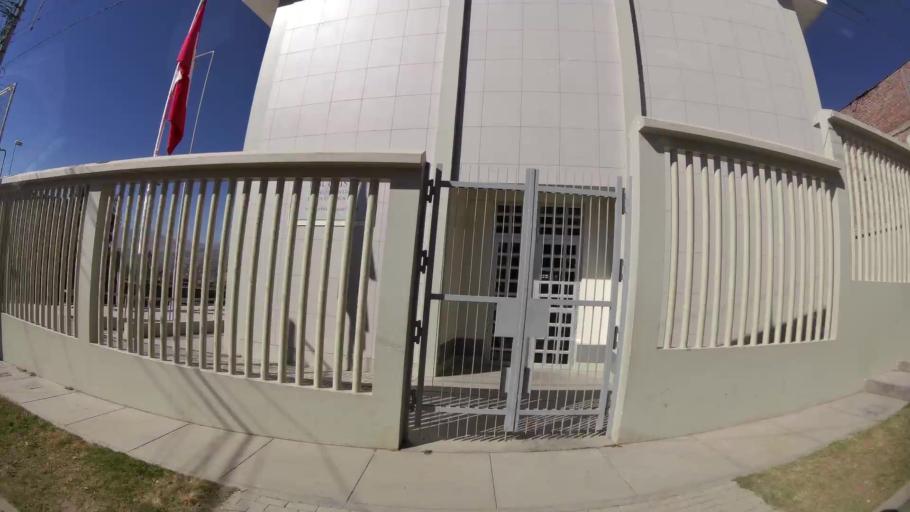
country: PE
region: Ayacucho
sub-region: Provincia de Huamanga
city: Ayacucho
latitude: -13.1632
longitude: -74.2338
